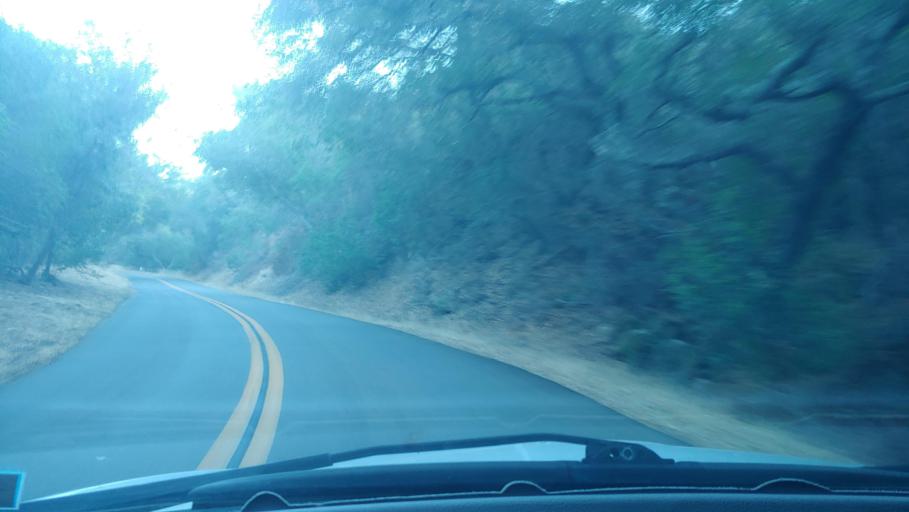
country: US
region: California
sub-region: Santa Barbara County
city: Goleta
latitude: 34.5326
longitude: -119.8409
